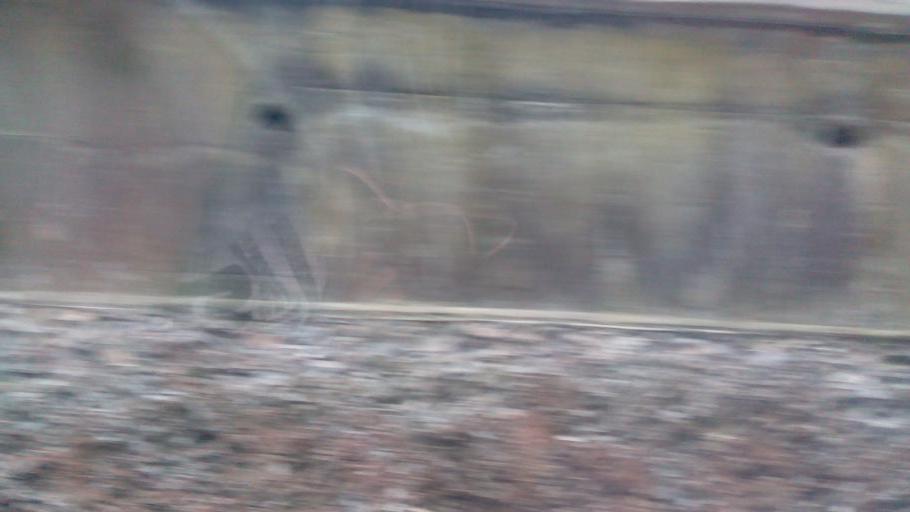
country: TW
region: Taiwan
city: Daxi
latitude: 24.4636
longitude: 121.3946
